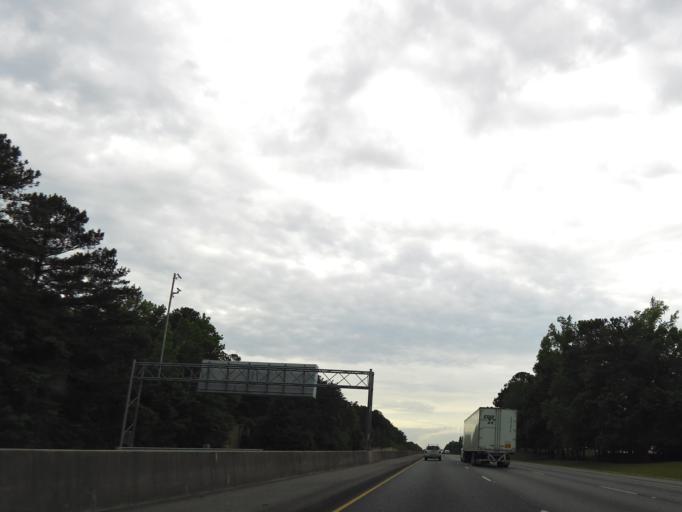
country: US
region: Georgia
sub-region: Bibb County
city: West Point
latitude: 32.8653
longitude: -83.7530
